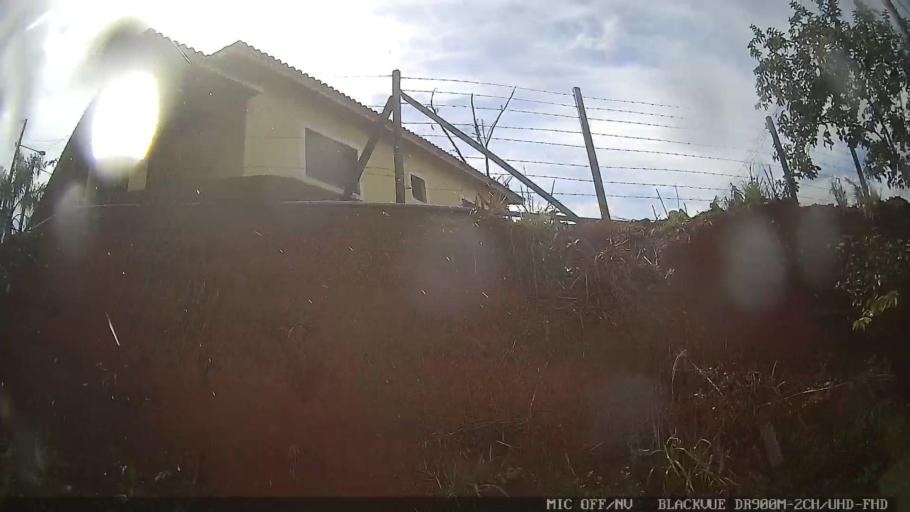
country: BR
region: Sao Paulo
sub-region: Jarinu
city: Jarinu
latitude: -23.0308
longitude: -46.6385
